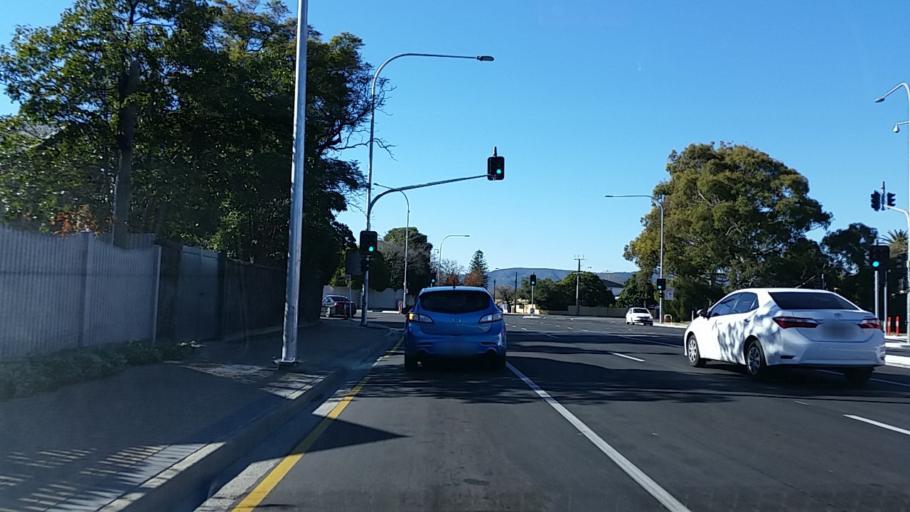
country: AU
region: South Australia
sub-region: Prospect
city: Prospect
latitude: -34.8932
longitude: 138.6089
